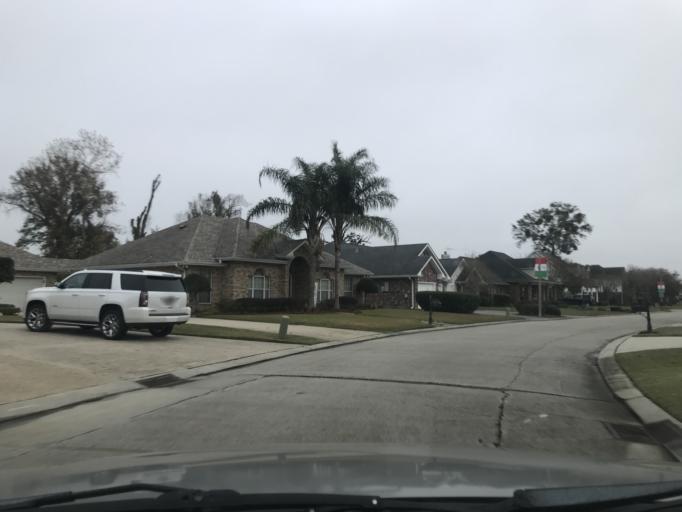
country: US
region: Louisiana
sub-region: Jefferson Parish
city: Woodmere
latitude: 29.8730
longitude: -90.0918
